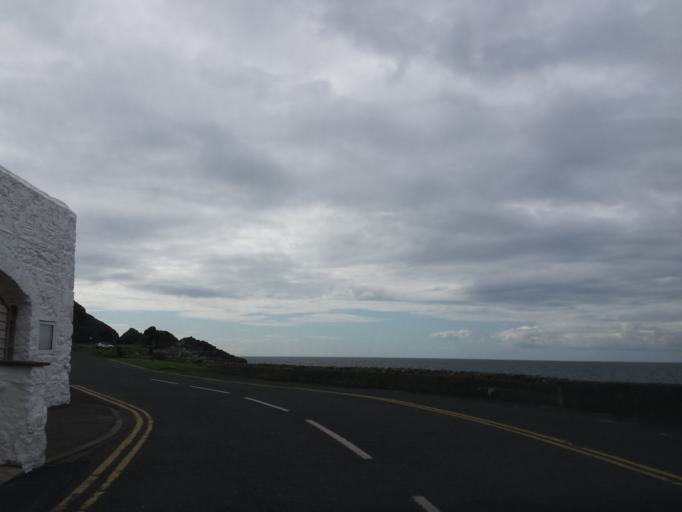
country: GB
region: Scotland
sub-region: Dumfries and Galloway
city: Stranraer
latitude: 54.8399
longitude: -5.1169
